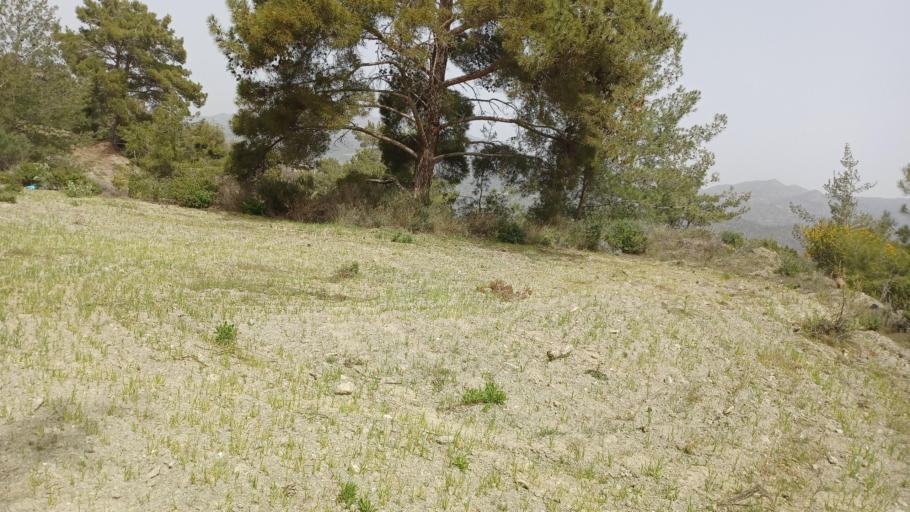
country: CY
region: Limassol
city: Parekklisha
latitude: 34.8285
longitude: 33.0956
